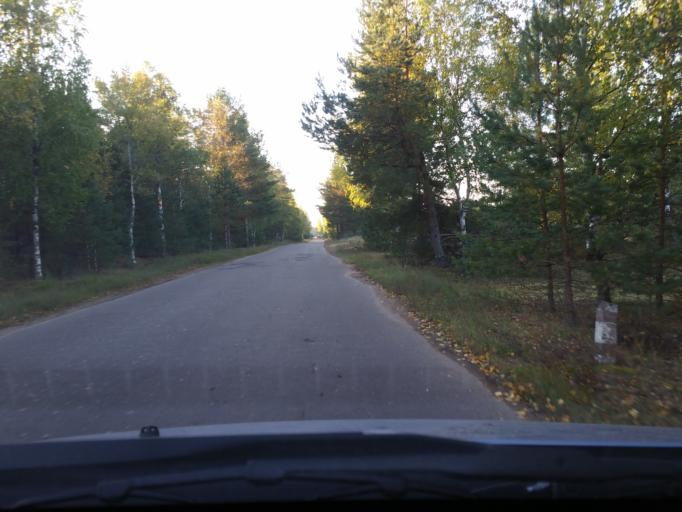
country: LV
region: Adazi
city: Adazi
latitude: 57.1128
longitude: 24.3629
